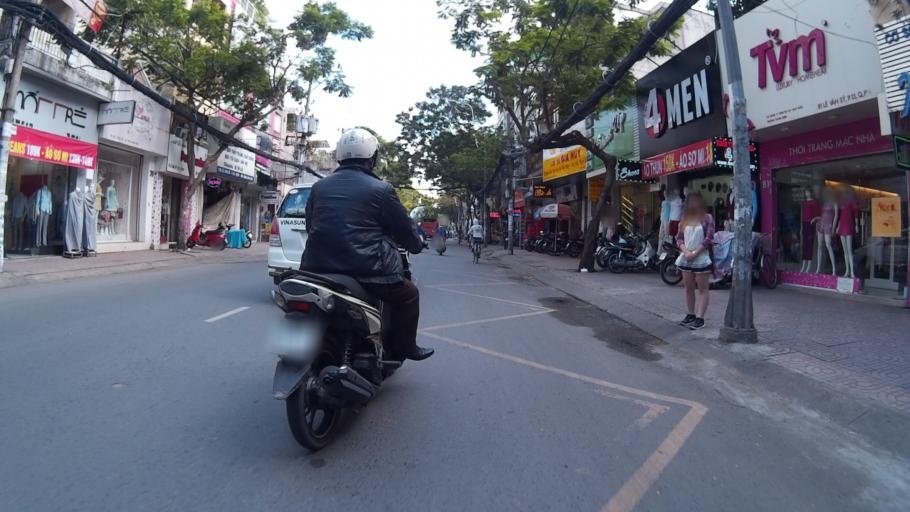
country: VN
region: Ho Chi Minh City
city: Quan Phu Nhuan
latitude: 10.7912
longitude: 106.6724
